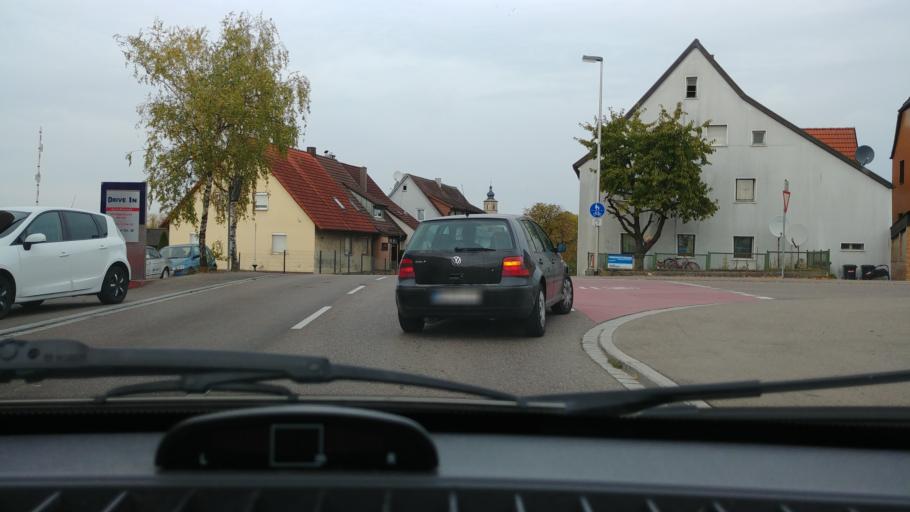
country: DE
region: Baden-Wuerttemberg
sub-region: Regierungsbezirk Stuttgart
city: Crailsheim
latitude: 49.1317
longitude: 10.0763
